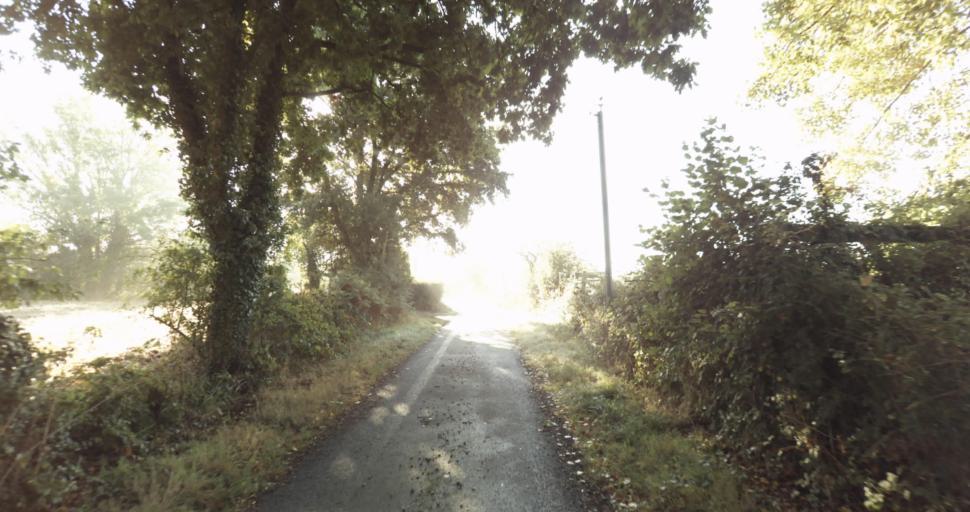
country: FR
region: Lower Normandy
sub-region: Departement de l'Orne
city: Vimoutiers
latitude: 48.9110
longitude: 0.1618
